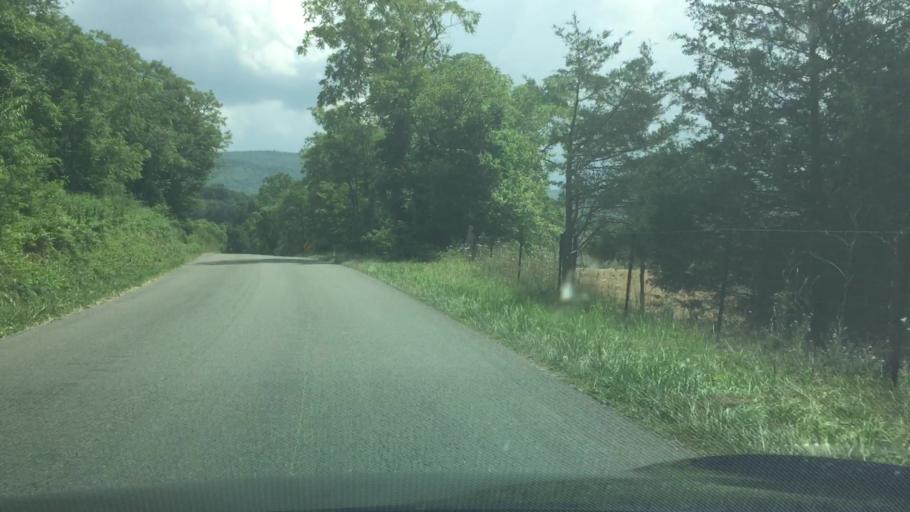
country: US
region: Virginia
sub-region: Wythe County
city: Wytheville
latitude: 36.9379
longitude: -81.0266
